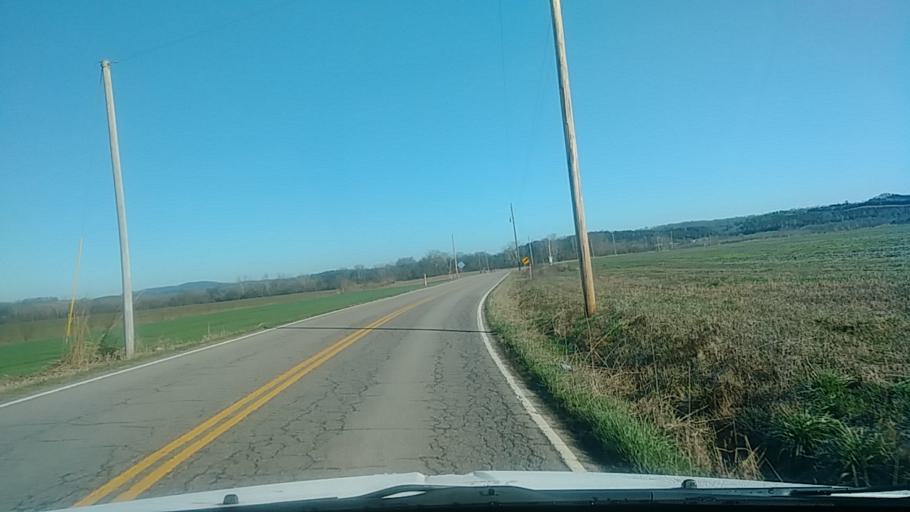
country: US
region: Tennessee
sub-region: Jefferson County
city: White Pine
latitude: 36.1637
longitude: -83.1628
